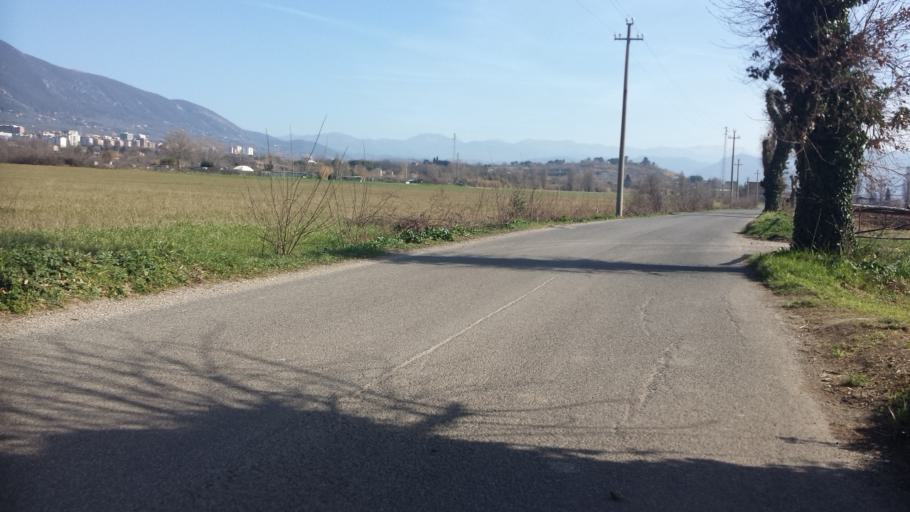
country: IT
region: Umbria
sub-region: Provincia di Terni
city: San Gemini
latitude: 42.5804
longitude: 12.5819
